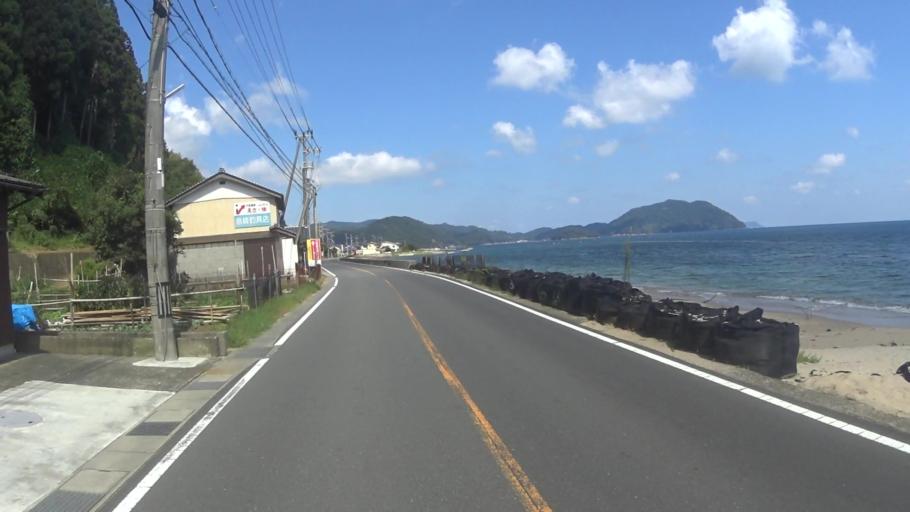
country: JP
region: Kyoto
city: Miyazu
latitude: 35.6526
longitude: 135.2556
